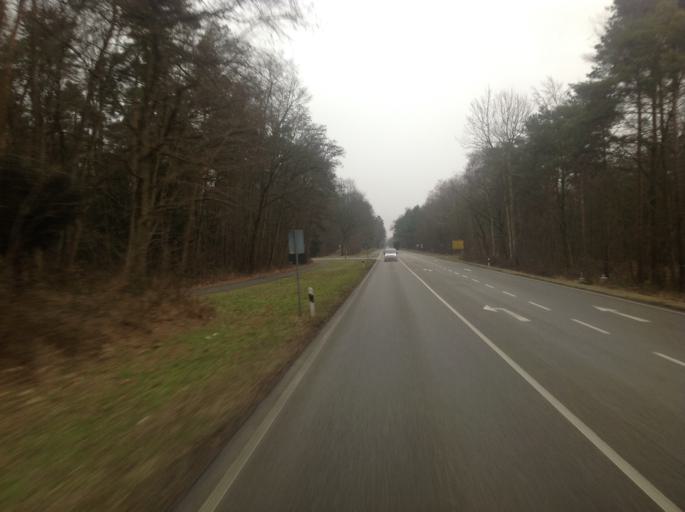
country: DE
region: Baden-Wuerttemberg
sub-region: Karlsruhe Region
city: Rastatt
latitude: 48.8340
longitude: 8.1803
